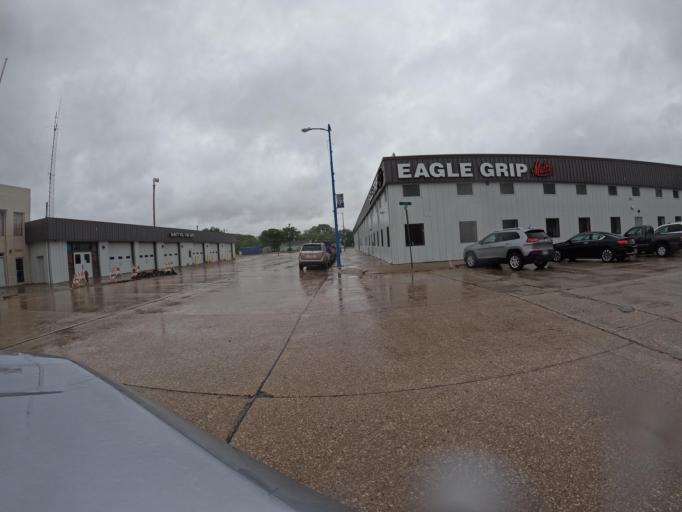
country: US
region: Nebraska
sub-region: Saline County
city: Wilber
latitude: 40.3945
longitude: -96.9192
